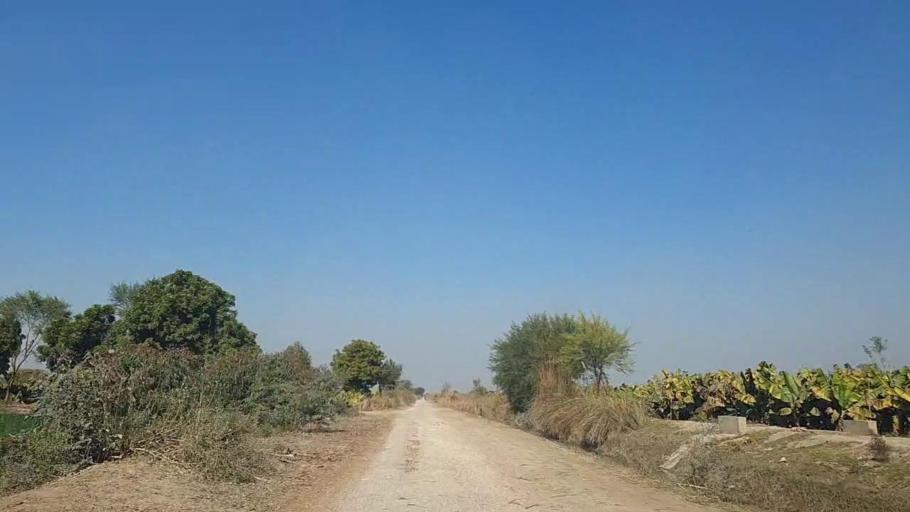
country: PK
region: Sindh
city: Sakrand
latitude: 26.2554
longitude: 68.2208
